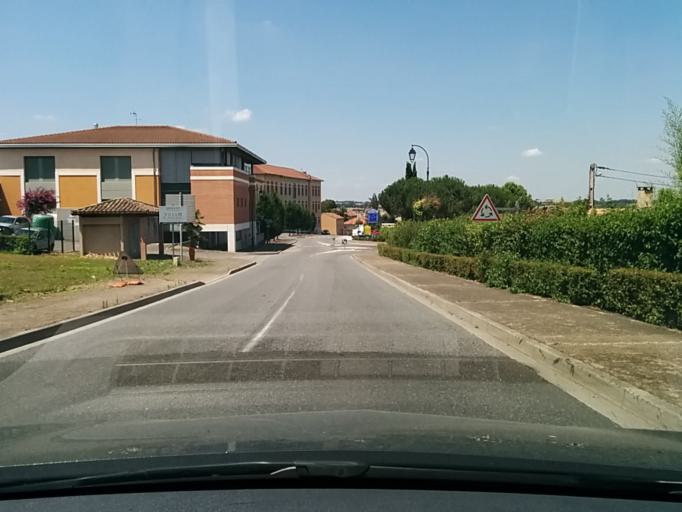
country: FR
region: Midi-Pyrenees
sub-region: Departement du Gers
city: Gimont
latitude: 43.6241
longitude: 0.8817
